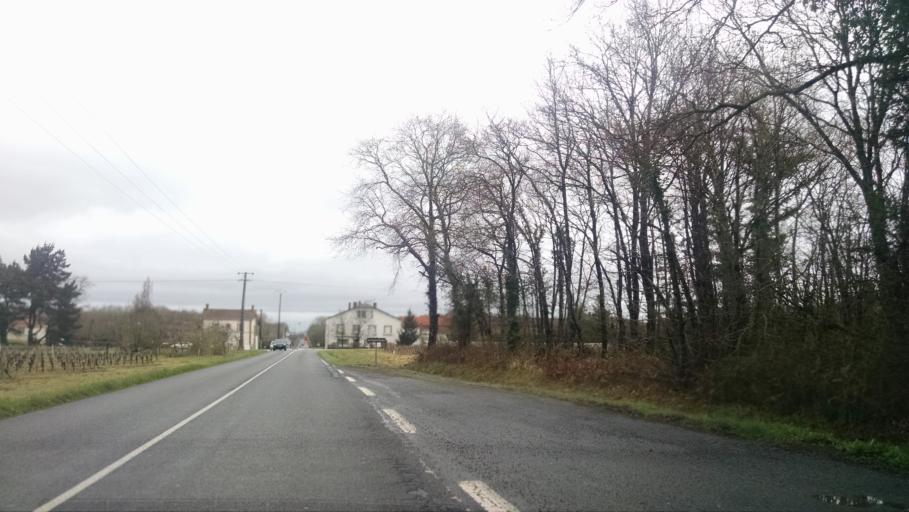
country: FR
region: Pays de la Loire
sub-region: Departement de la Loire-Atlantique
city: Monnieres
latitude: 47.1176
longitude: -1.3653
